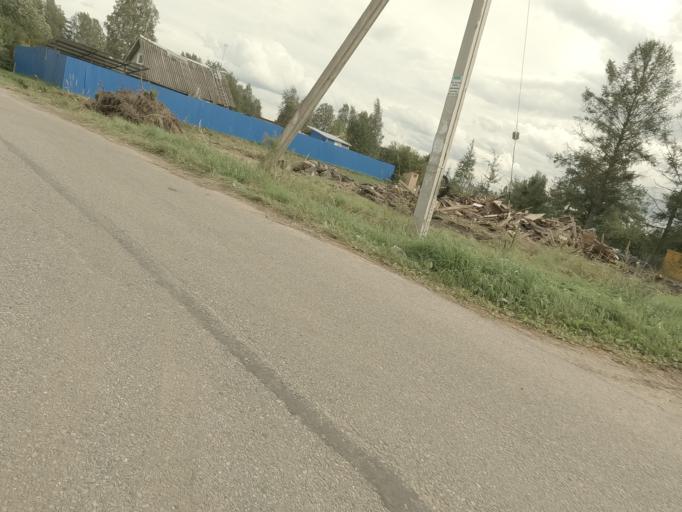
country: RU
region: Leningrad
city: Mga
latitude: 59.7601
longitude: 31.0333
